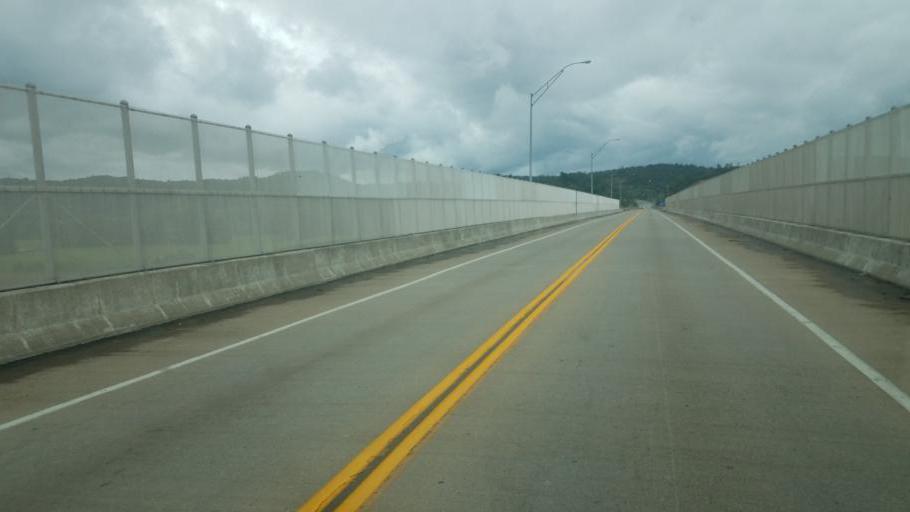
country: US
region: Ohio
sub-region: Scioto County
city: Franklin Furnace
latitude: 38.6468
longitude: -82.8634
